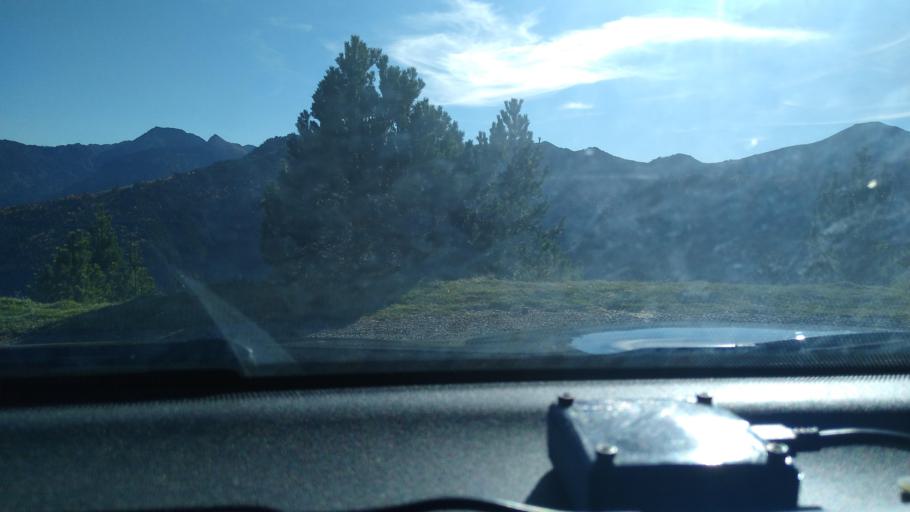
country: FR
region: Midi-Pyrenees
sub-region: Departement de l'Ariege
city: Ax-les-Thermes
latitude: 42.7346
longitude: 2.0017
